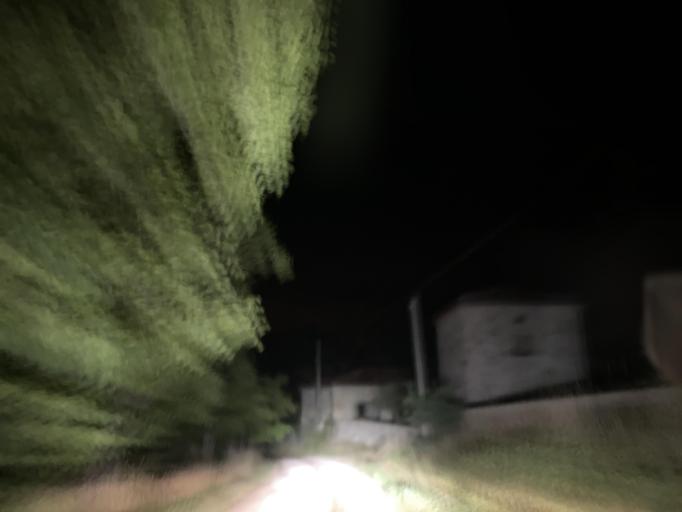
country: FR
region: Auvergne
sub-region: Departement du Puy-de-Dome
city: Peschadoires
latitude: 45.7725
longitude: 3.4839
